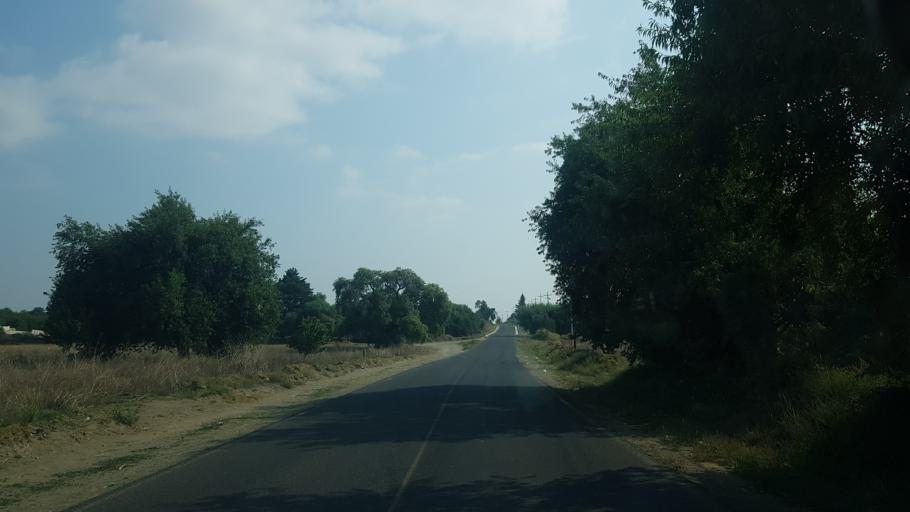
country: MX
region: Puebla
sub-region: Huejotzingo
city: San Juan Pancoac
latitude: 19.1277
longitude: -98.4199
